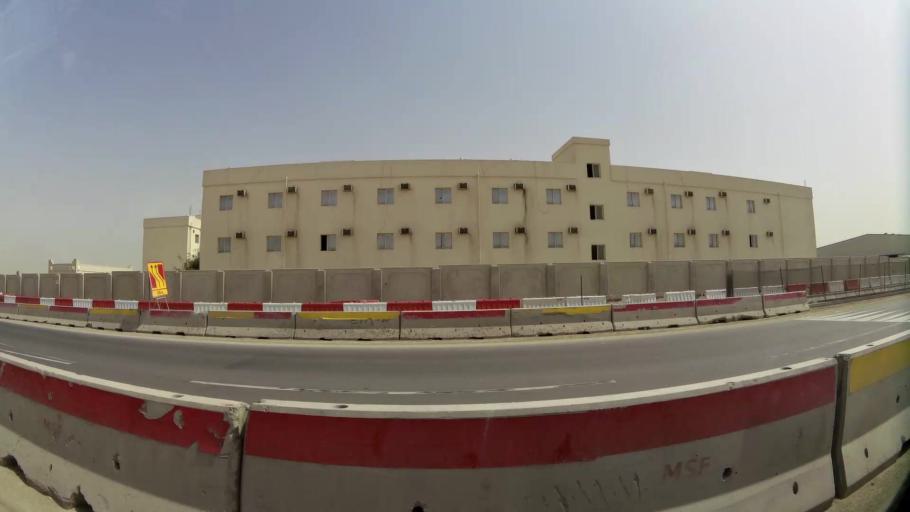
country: QA
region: Baladiyat ar Rayyan
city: Ar Rayyan
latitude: 25.1932
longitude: 51.4182
